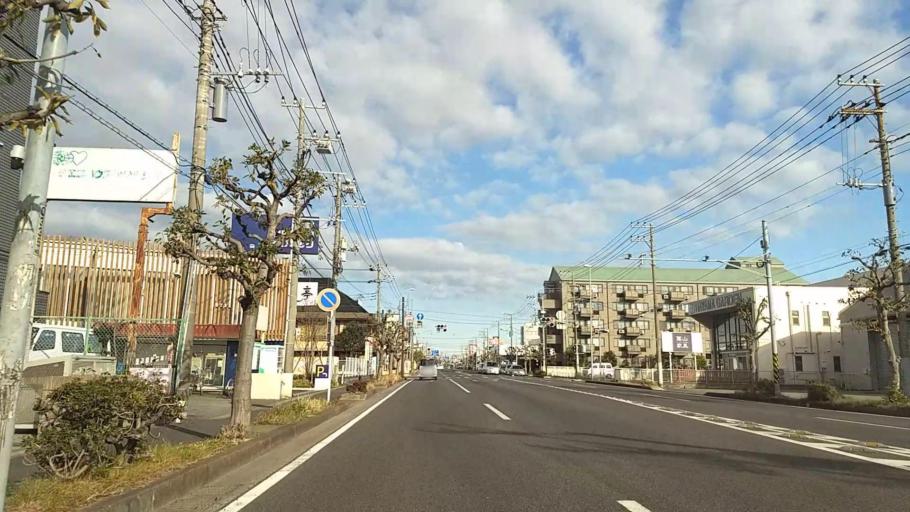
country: JP
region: Kanagawa
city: Hiratsuka
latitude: 35.3426
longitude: 139.3562
